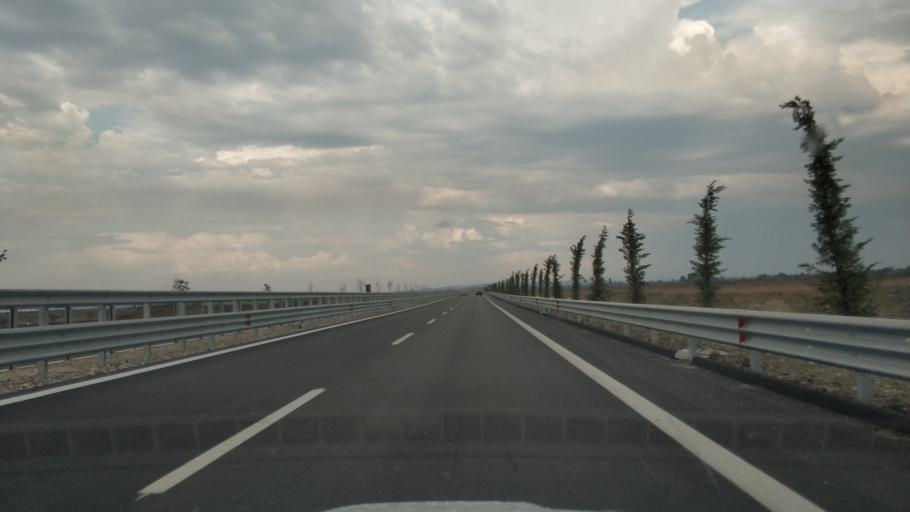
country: AL
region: Fier
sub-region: Rrethi i Fierit
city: Topoje
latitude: 40.7326
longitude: 19.4450
